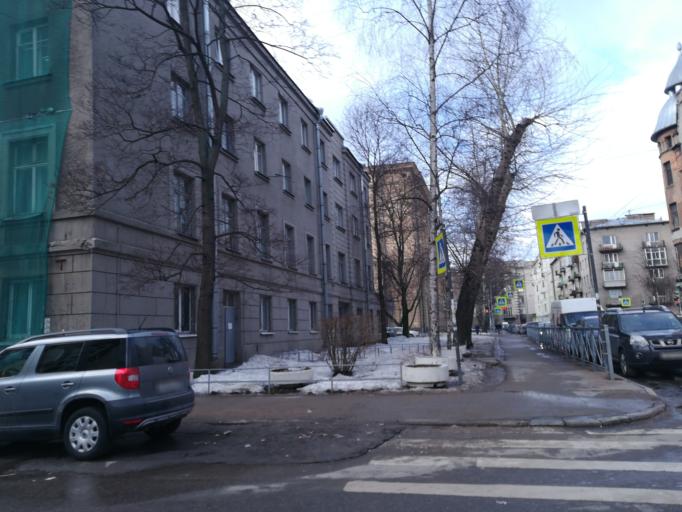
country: RU
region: St.-Petersburg
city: Petrogradka
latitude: 59.9605
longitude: 30.3228
